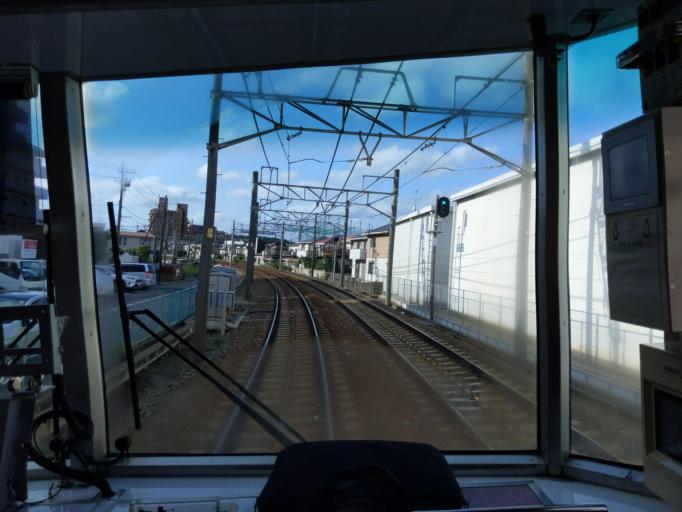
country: JP
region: Chiba
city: Kashiwa
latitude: 35.8005
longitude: 139.9641
